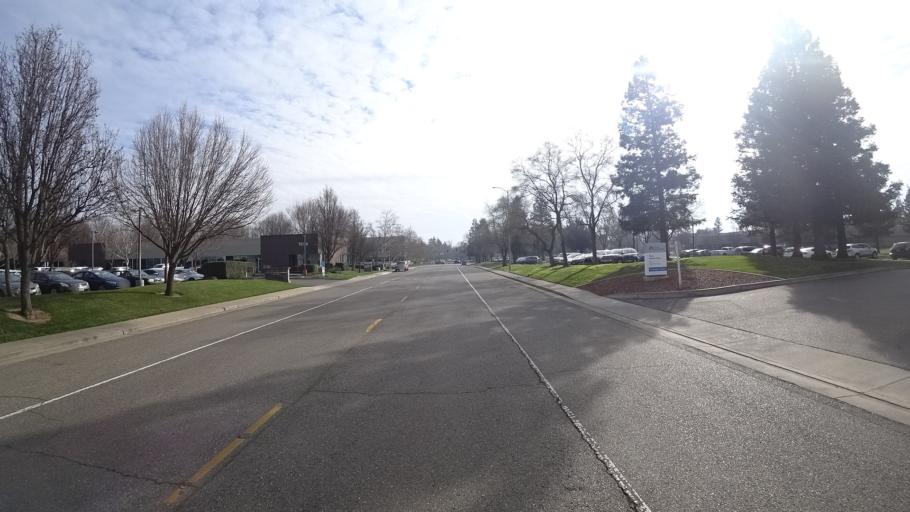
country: US
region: California
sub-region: Yolo County
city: Davis
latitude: 38.5417
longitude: -121.7273
